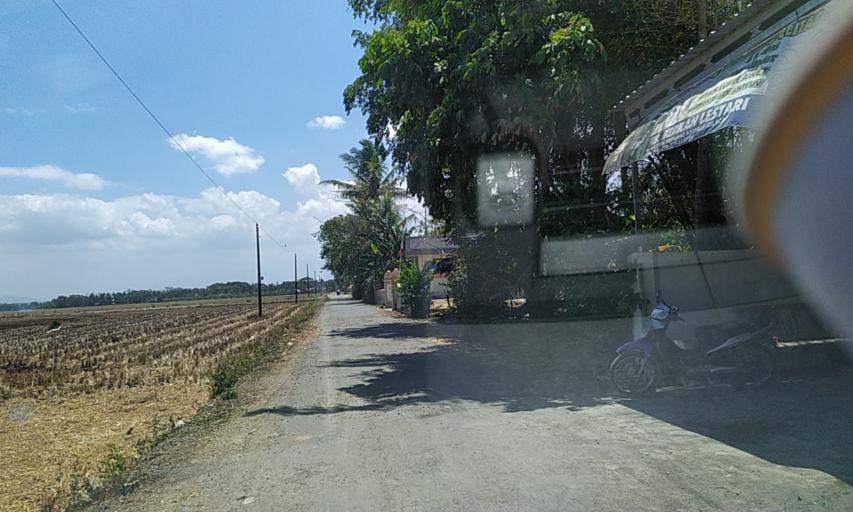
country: ID
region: Central Java
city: Mernek
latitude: -7.6377
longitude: 109.1743
